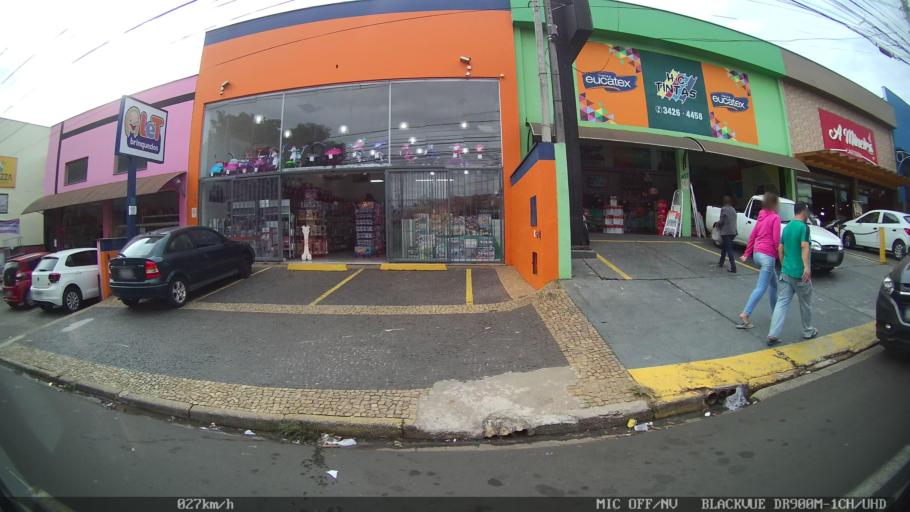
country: BR
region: Sao Paulo
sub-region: Piracicaba
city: Piracicaba
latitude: -22.7388
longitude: -47.6263
